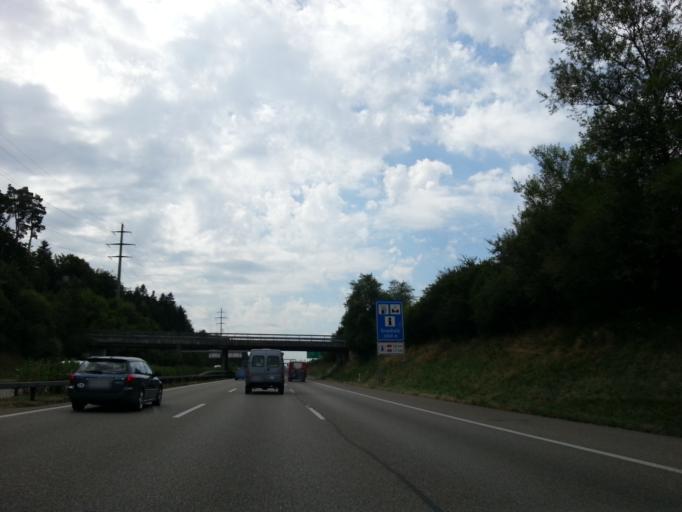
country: CH
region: Bern
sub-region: Bern-Mittelland District
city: Urtenen
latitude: 47.0060
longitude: 7.4946
